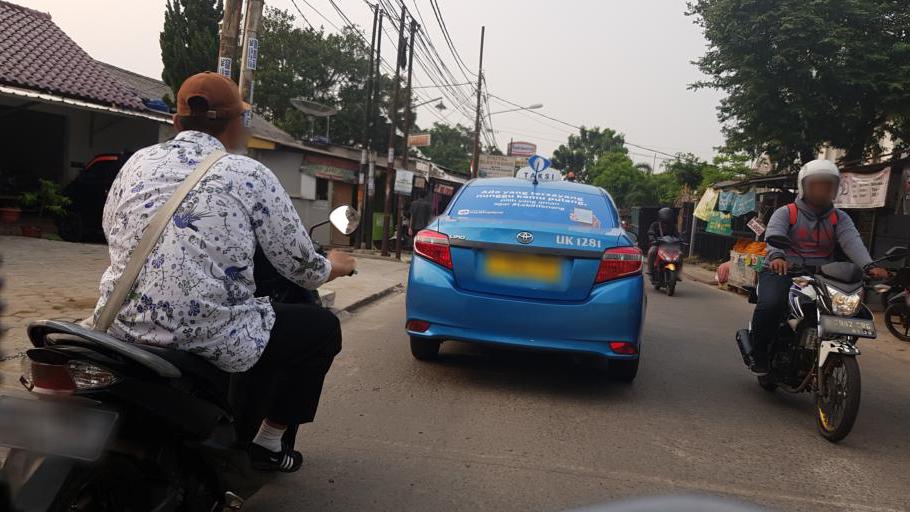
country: ID
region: West Java
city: Depok
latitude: -6.3703
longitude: 106.8426
